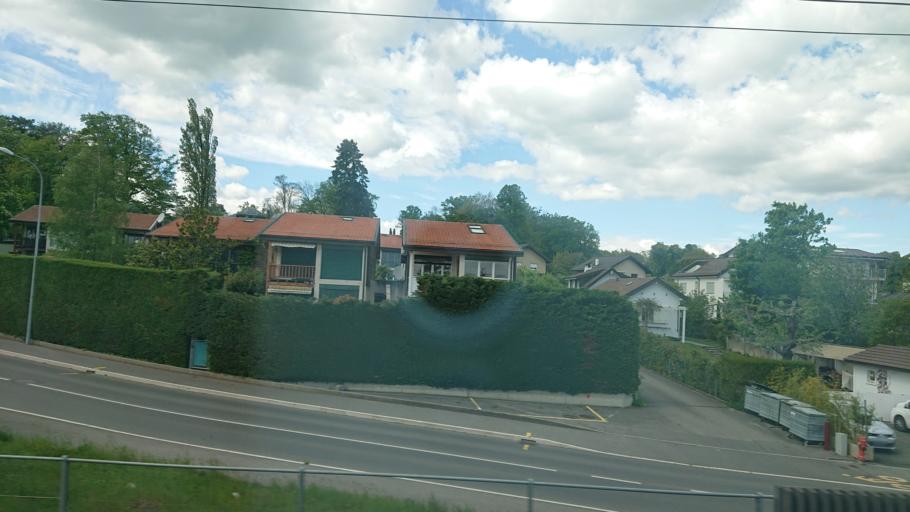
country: CH
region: Geneva
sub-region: Geneva
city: Bellevue
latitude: 46.2571
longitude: 6.1539
